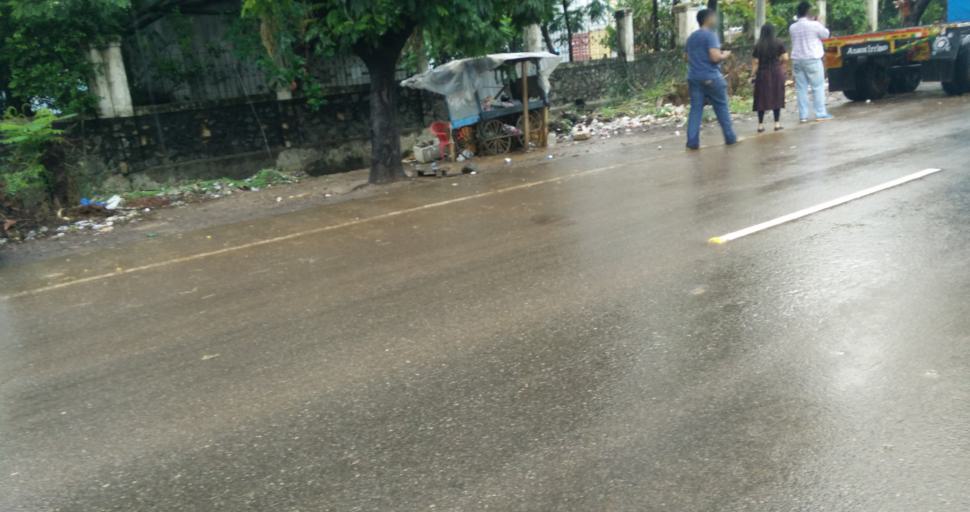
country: IN
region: Tamil Nadu
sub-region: Kancheepuram
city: Nandambakkam
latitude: 13.0003
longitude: 80.0062
